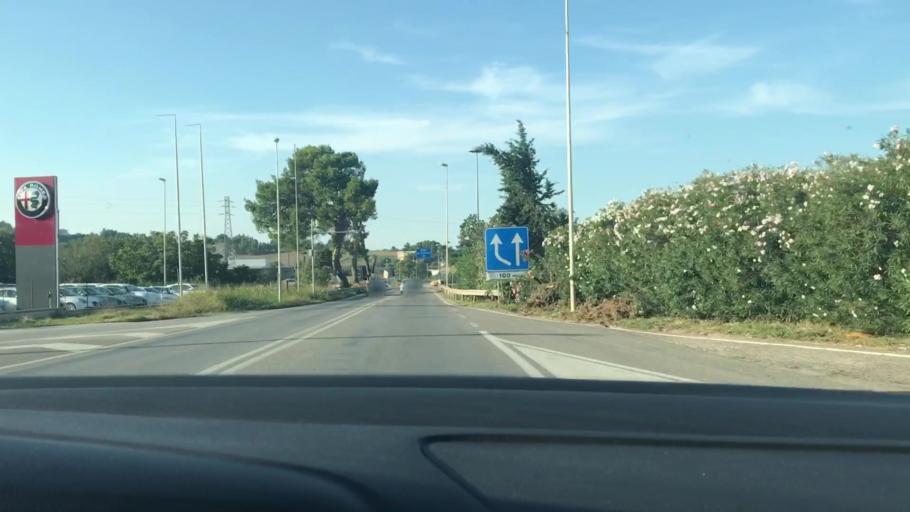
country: IT
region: Basilicate
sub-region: Provincia di Matera
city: Matera
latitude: 40.6857
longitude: 16.5902
